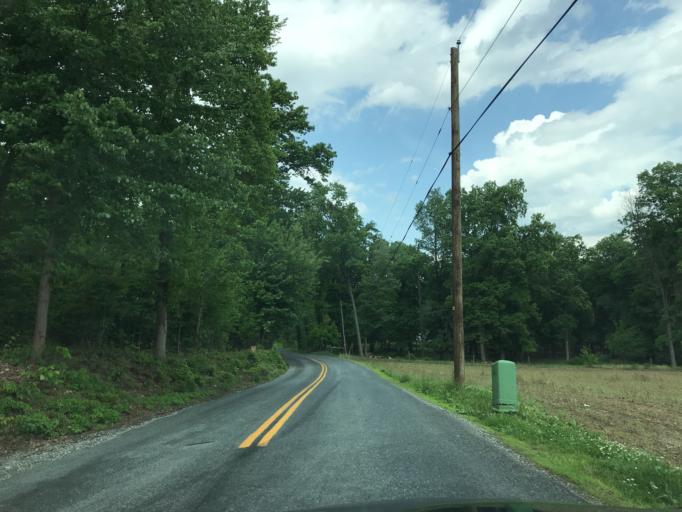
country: US
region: Pennsylvania
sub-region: York County
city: Susquehanna Trails
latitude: 39.7083
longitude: -76.3260
